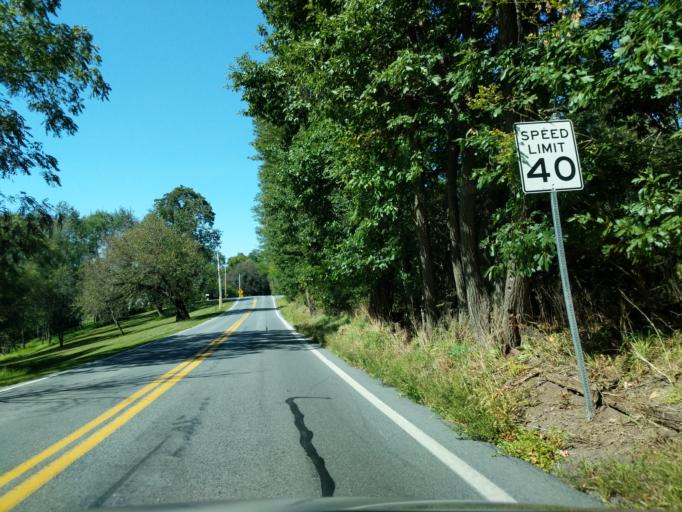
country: US
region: Pennsylvania
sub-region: Montgomery County
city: East Greenville
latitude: 40.4481
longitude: -75.4884
